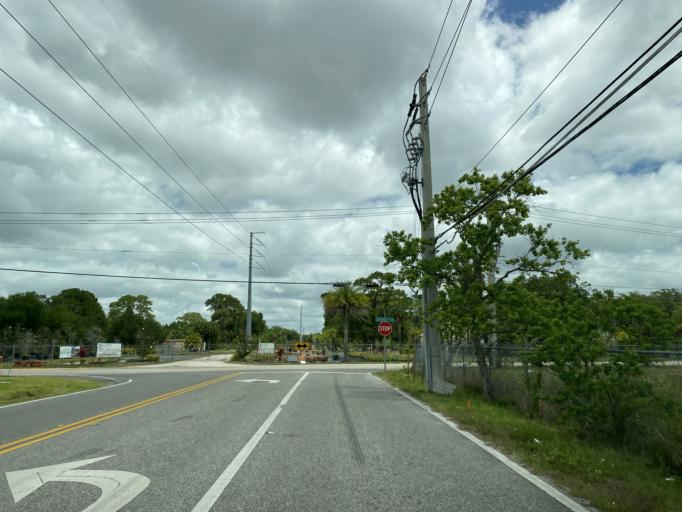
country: US
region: Florida
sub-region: Volusia County
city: DeBary
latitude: 28.8278
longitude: -81.3393
